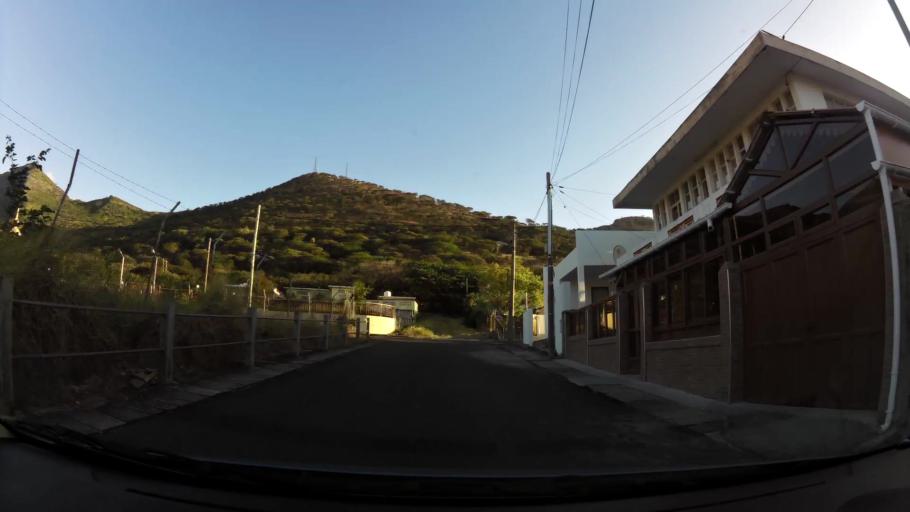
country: MU
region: Port Louis
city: Port Louis
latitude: -20.1754
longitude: 57.5068
